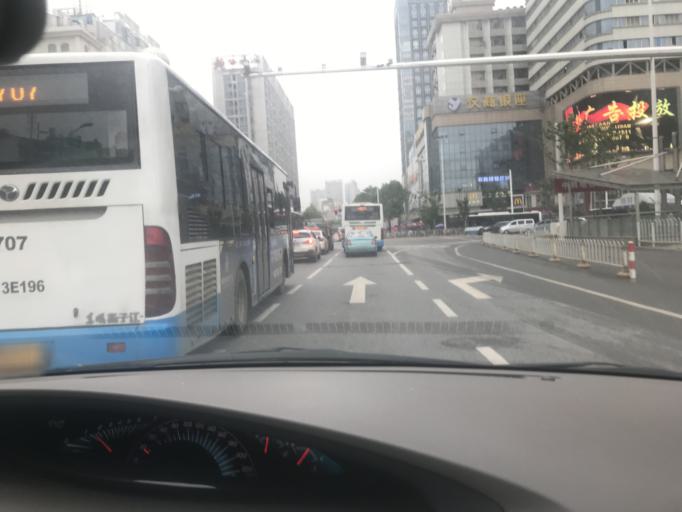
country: CN
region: Hubei
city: Wuhan
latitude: 30.5521
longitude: 114.2599
